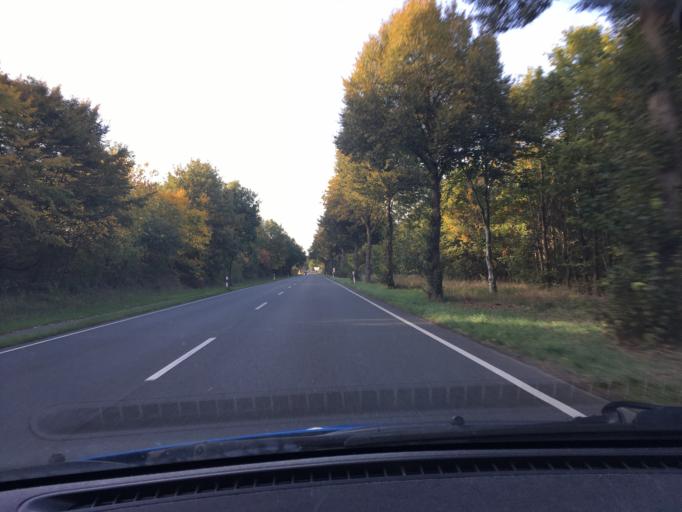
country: DE
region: Lower Saxony
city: Munster
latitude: 52.9775
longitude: 10.0989
